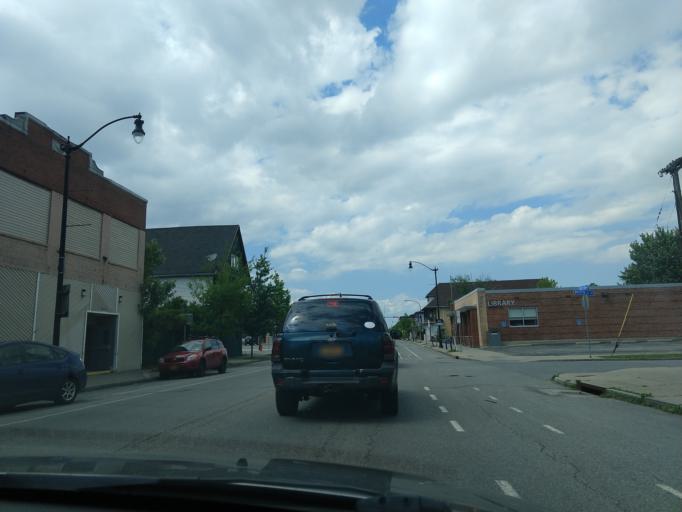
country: US
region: New York
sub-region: Erie County
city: Lackawanna
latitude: 42.8435
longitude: -78.8237
